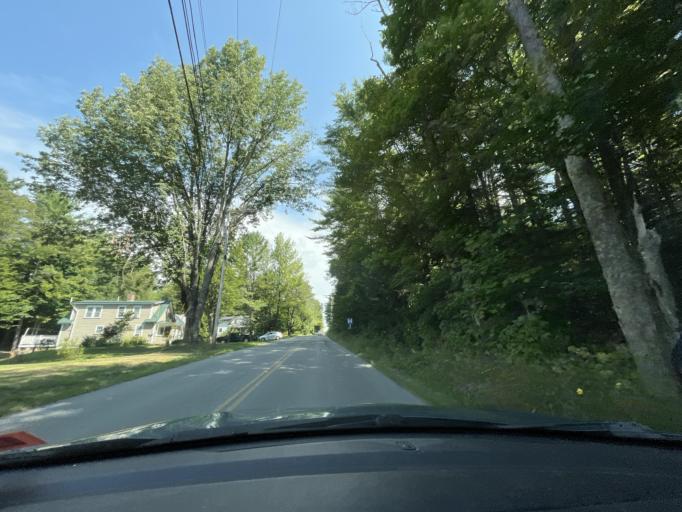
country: US
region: New Hampshire
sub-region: Merrimack County
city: New London
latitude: 43.4184
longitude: -72.0036
